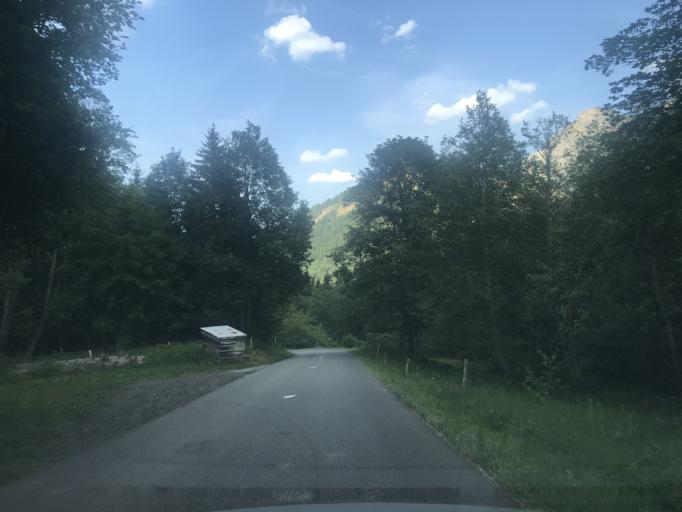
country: FR
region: Rhone-Alpes
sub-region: Departement de la Savoie
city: Saint-Etienne-de-Cuines
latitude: 45.2723
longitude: 6.2009
